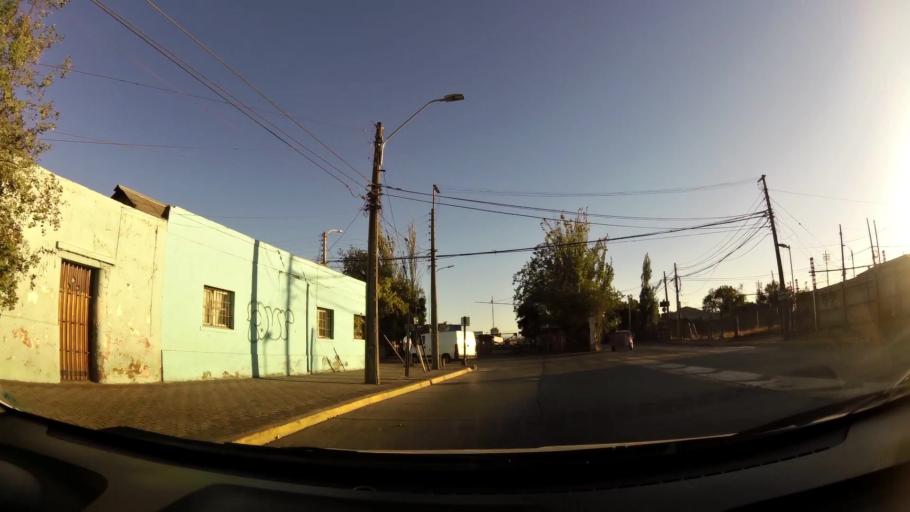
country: CL
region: O'Higgins
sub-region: Provincia de Cachapoal
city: Rancagua
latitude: -34.1729
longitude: -70.7530
